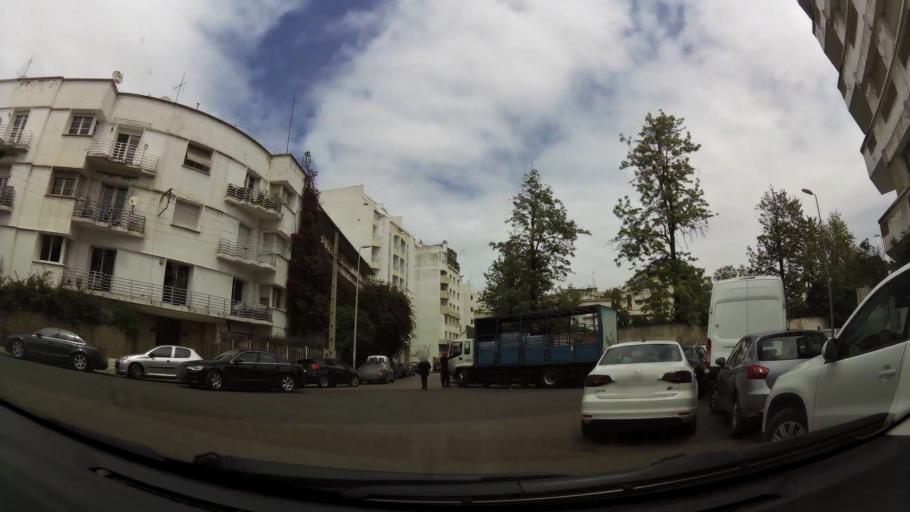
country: MA
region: Grand Casablanca
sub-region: Casablanca
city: Casablanca
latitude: 33.5877
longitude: -7.6287
